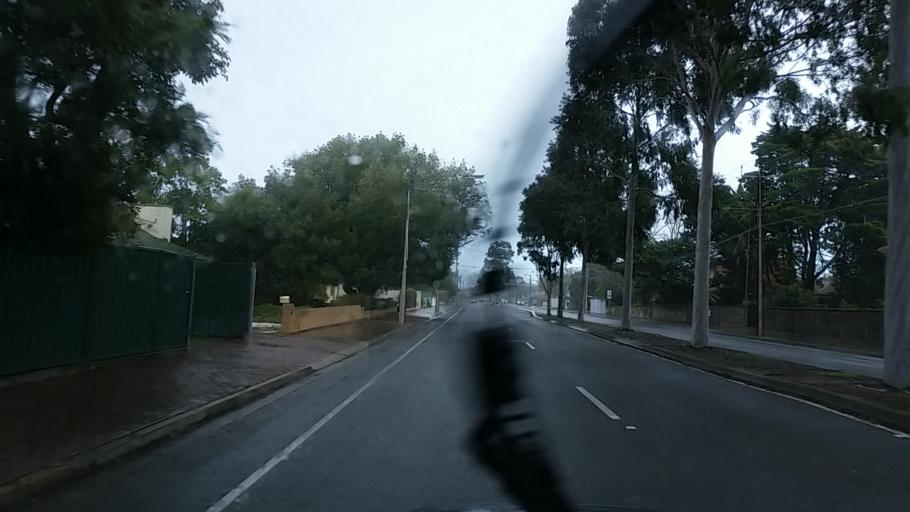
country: AU
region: South Australia
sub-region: Adelaide
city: Brighton
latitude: -35.0190
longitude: 138.5275
